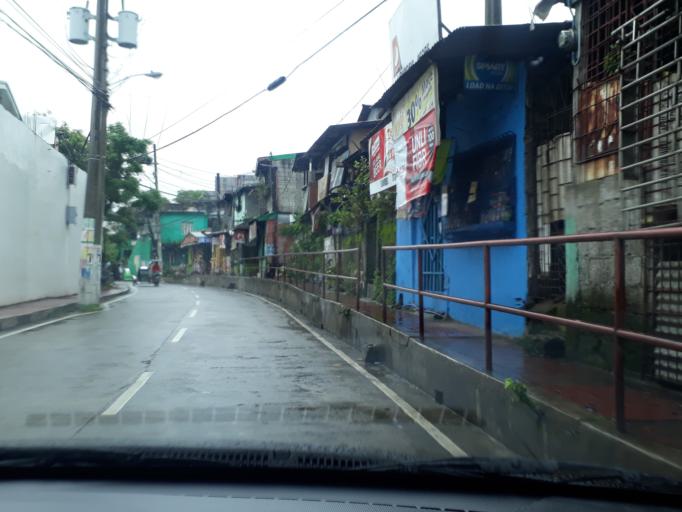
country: PH
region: Calabarzon
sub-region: Province of Rizal
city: Valenzuela
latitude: 14.7125
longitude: 120.9843
